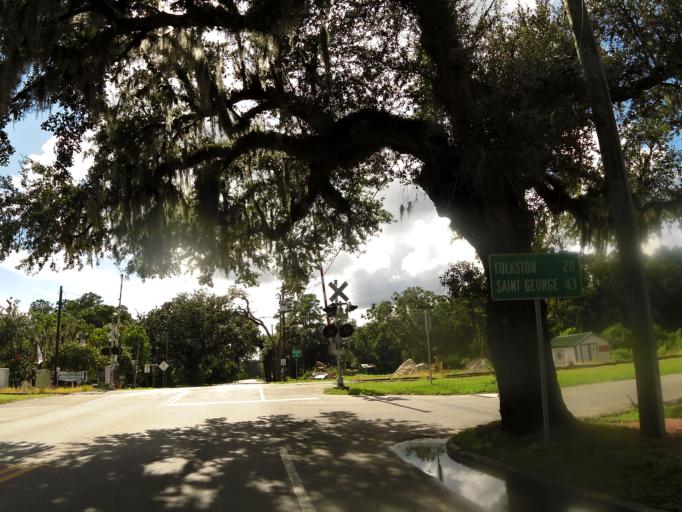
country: US
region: Georgia
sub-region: Camden County
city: Kingsland
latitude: 30.7999
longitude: -81.6908
